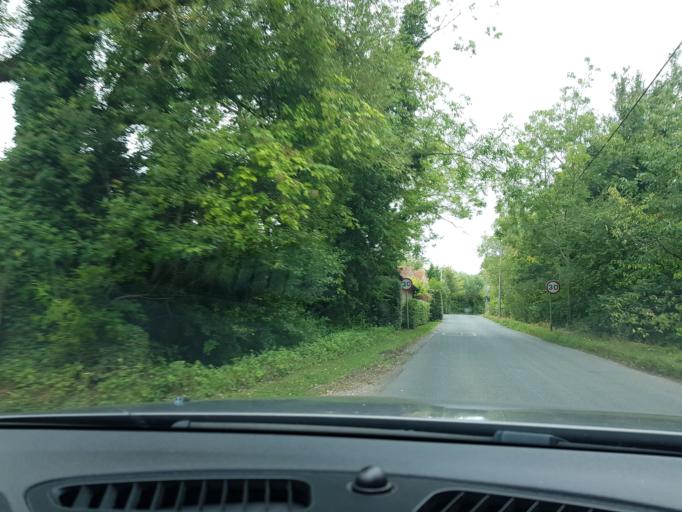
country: GB
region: England
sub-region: Wiltshire
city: Ramsbury
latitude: 51.4417
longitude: -1.5917
